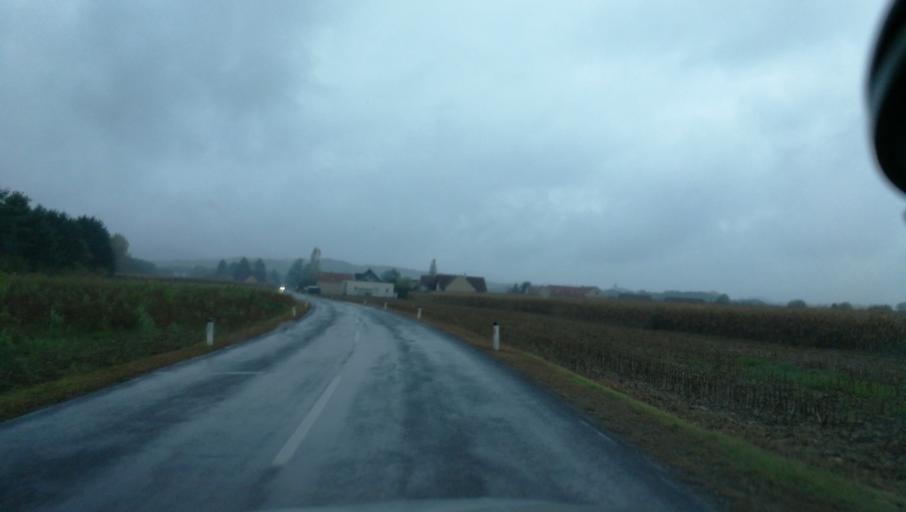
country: AT
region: Styria
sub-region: Politischer Bezirk Leibnitz
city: Sankt Veit am Vogau
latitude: 46.7386
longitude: 15.6139
